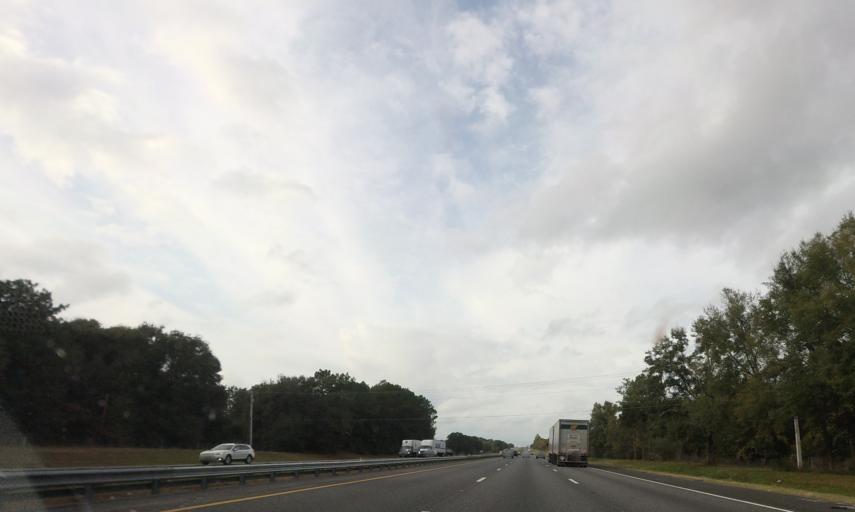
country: US
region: Florida
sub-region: Columbia County
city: Lake City
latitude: 30.1943
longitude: -82.6959
